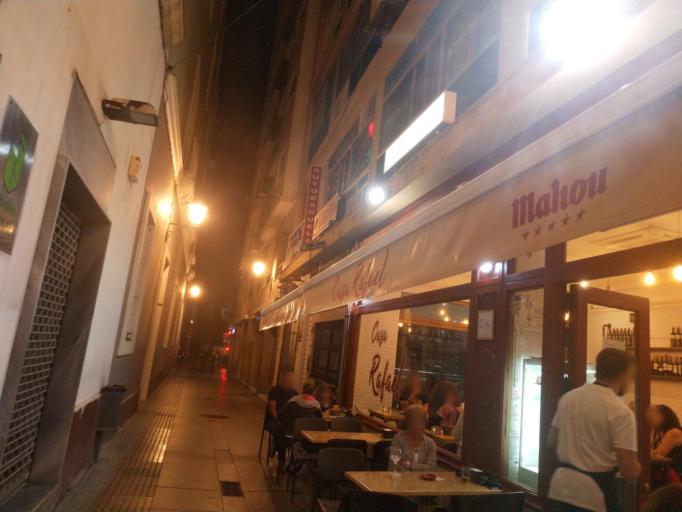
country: ES
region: Andalusia
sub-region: Provincia de Cadiz
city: Cadiz
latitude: 36.5334
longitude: -6.2941
